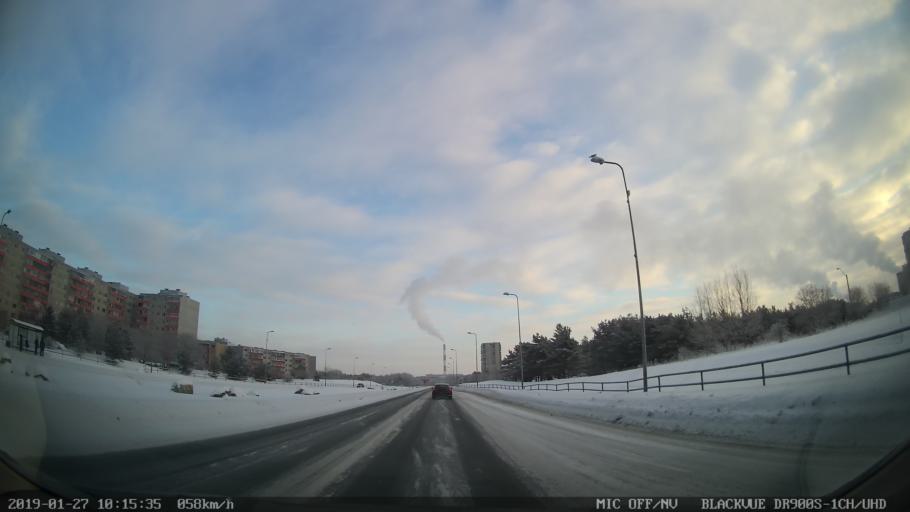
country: EE
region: Harju
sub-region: Tallinna linn
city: Kose
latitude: 59.4451
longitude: 24.8908
